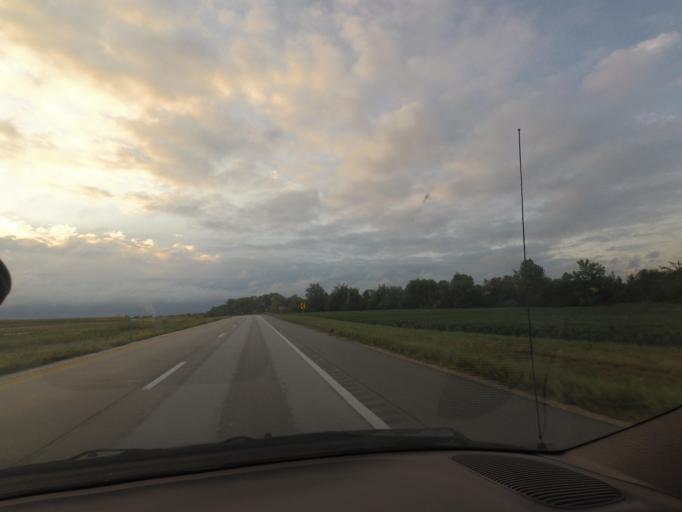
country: US
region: Missouri
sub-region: Shelby County
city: Shelbina
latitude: 39.6905
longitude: -92.0216
